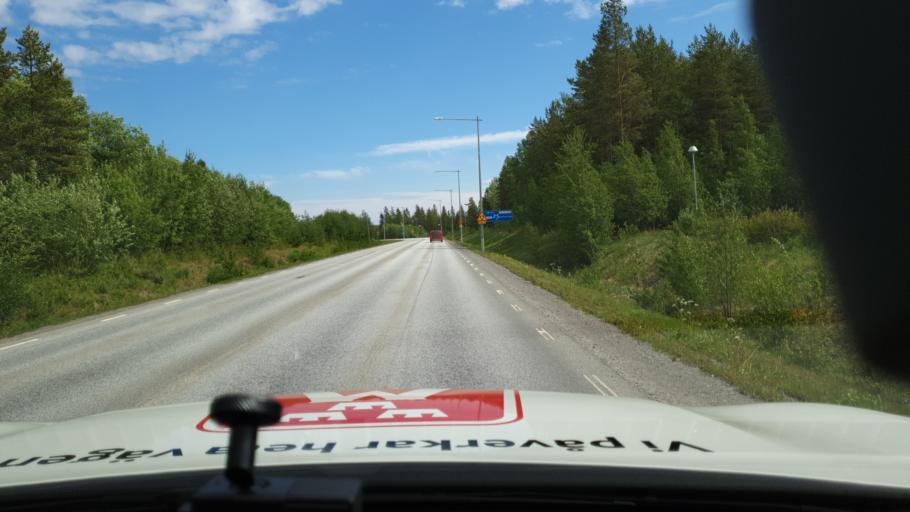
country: SE
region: Vaesterbotten
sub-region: Umea Kommun
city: Ersmark
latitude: 63.8024
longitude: 20.3565
